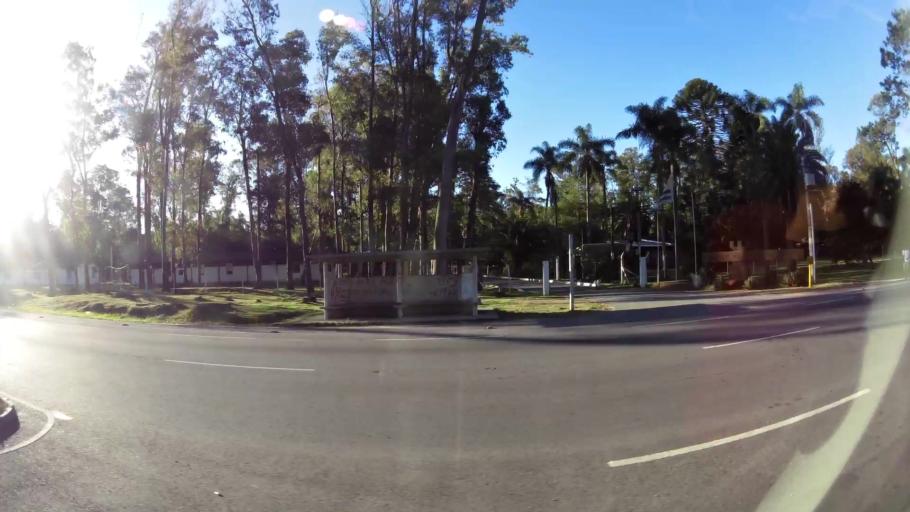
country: UY
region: Canelones
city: Paso de Carrasco
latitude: -34.8507
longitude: -56.0360
